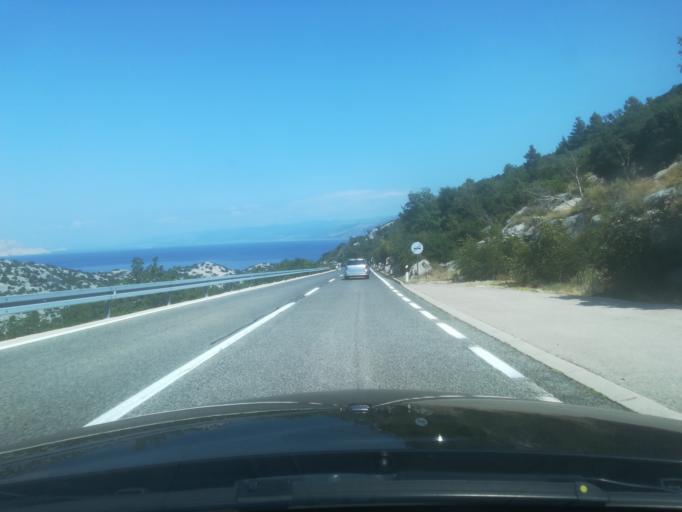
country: HR
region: Licko-Senjska
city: Senj
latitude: 44.8949
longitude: 14.9123
